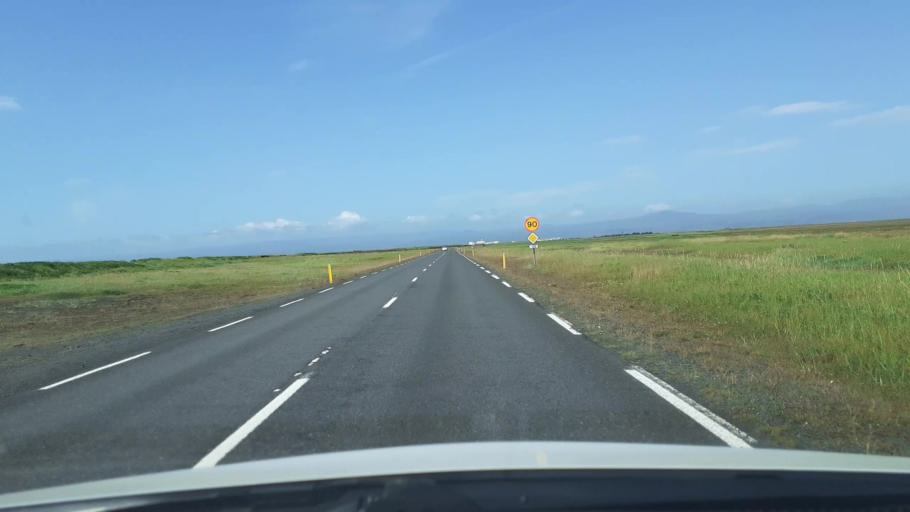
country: IS
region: South
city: Selfoss
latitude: 63.8428
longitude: -21.0848
